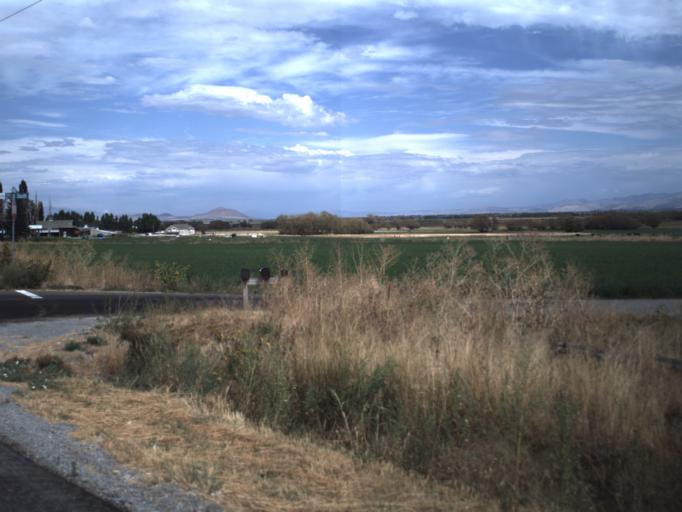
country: US
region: Utah
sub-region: Cache County
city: Mendon
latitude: 41.6800
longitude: -111.9610
